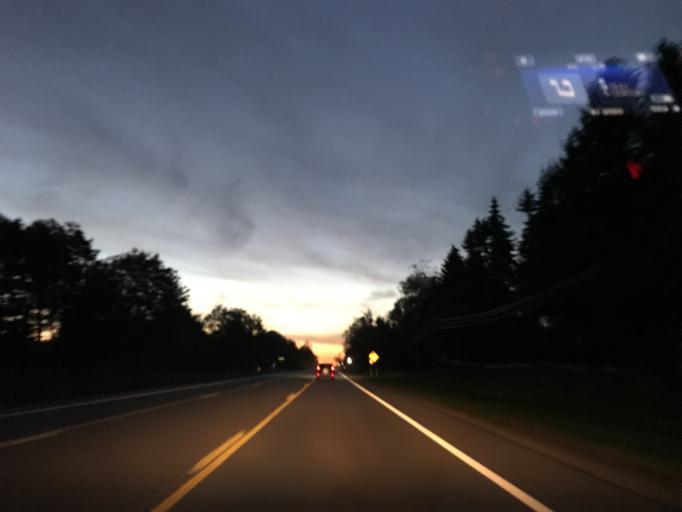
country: US
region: Michigan
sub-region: Wayne County
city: Northville
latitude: 42.4369
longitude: -83.5006
